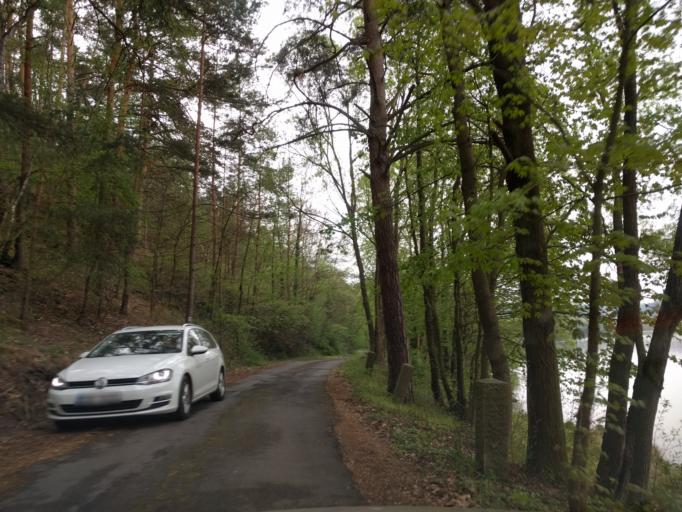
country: CZ
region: Central Bohemia
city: Krasna Hora nad Vltavou
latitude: 49.6719
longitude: 14.2634
